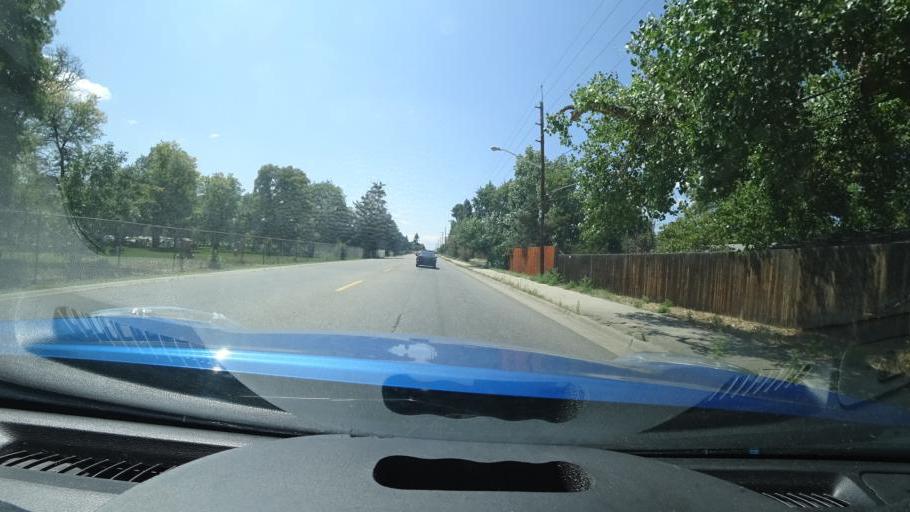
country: US
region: Colorado
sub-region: Arapahoe County
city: Glendale
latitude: 39.7064
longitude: -104.9035
